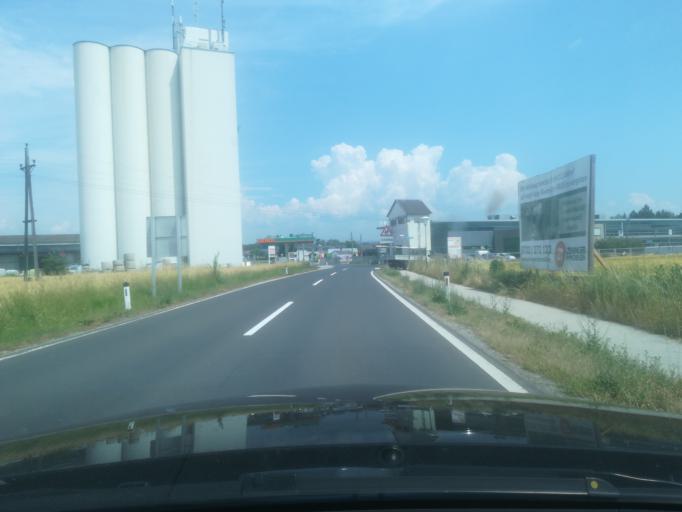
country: AT
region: Upper Austria
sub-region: Politischer Bezirk Urfahr-Umgebung
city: Goldworth
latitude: 48.2868
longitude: 14.1165
